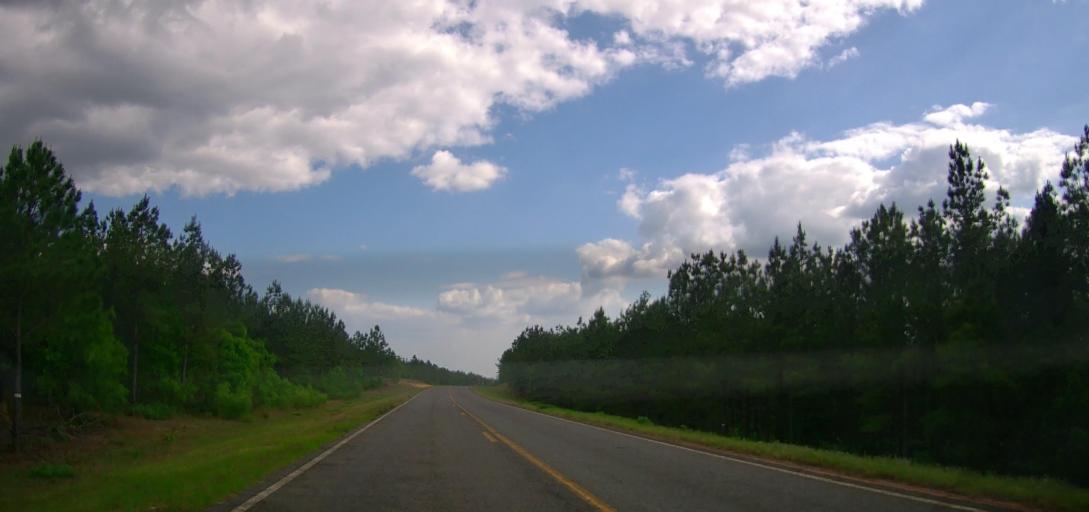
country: US
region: Georgia
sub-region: Johnson County
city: Wrightsville
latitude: 32.7553
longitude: -82.9276
